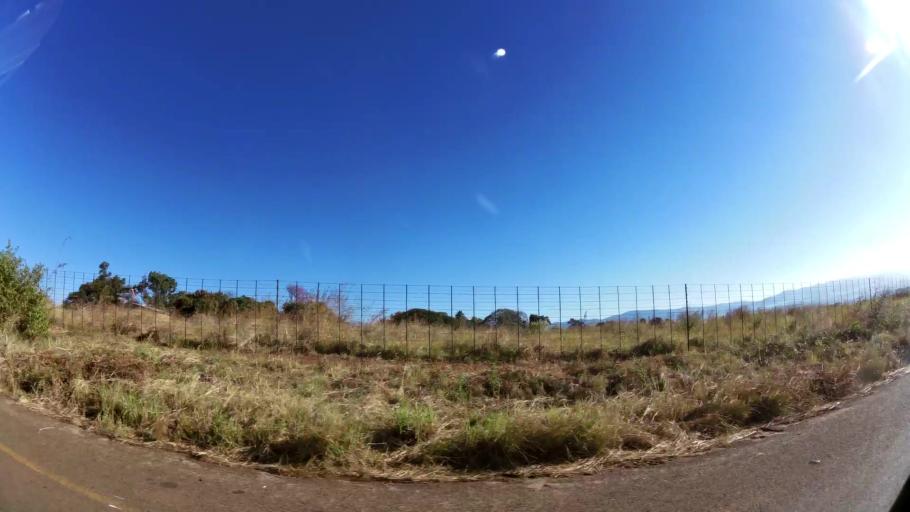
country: ZA
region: Limpopo
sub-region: Mopani District Municipality
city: Tzaneen
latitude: -23.8381
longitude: 30.1329
